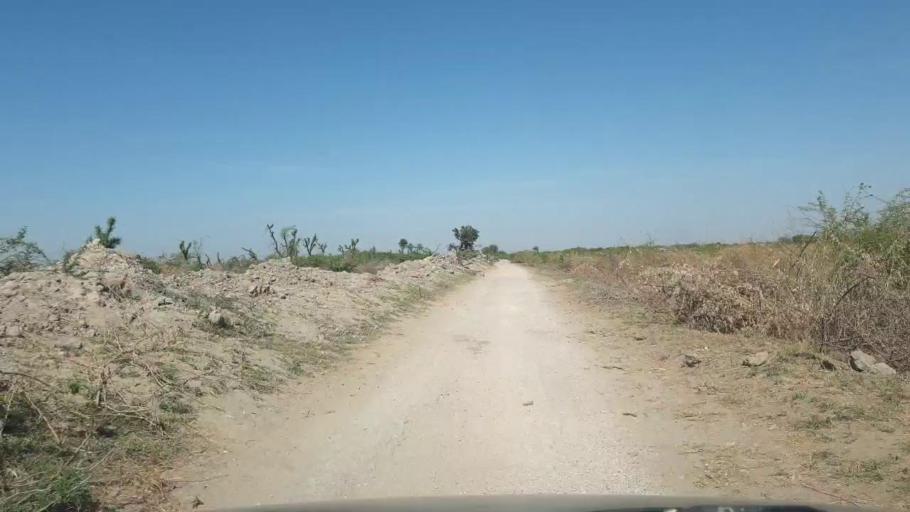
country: PK
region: Sindh
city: Dhoro Naro
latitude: 25.4051
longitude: 69.6139
